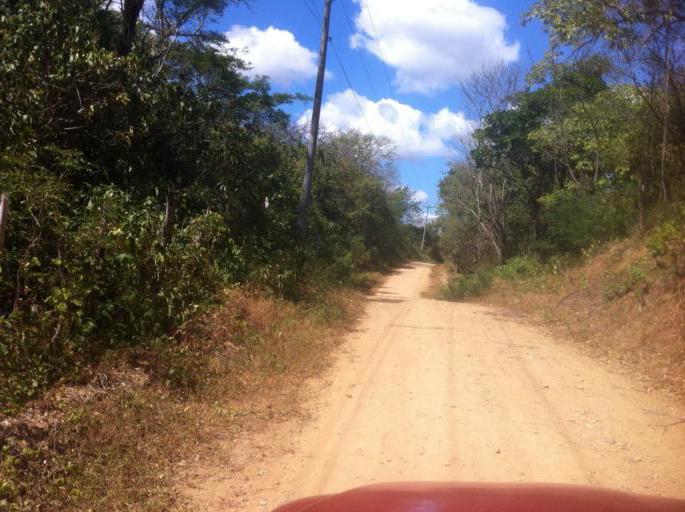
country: NI
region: Rivas
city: Tola
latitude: 11.3497
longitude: -85.9576
